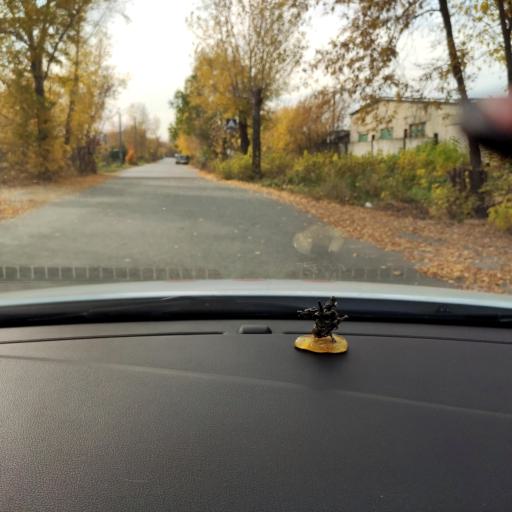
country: RU
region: Tatarstan
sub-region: Gorod Kazan'
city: Kazan
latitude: 55.7471
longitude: 49.1121
